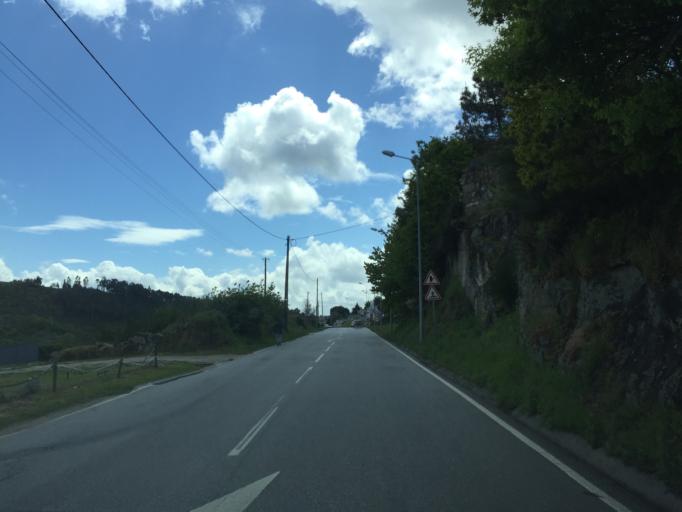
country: PT
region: Viseu
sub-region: Viseu
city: Viseu
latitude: 40.6520
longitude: -7.9478
